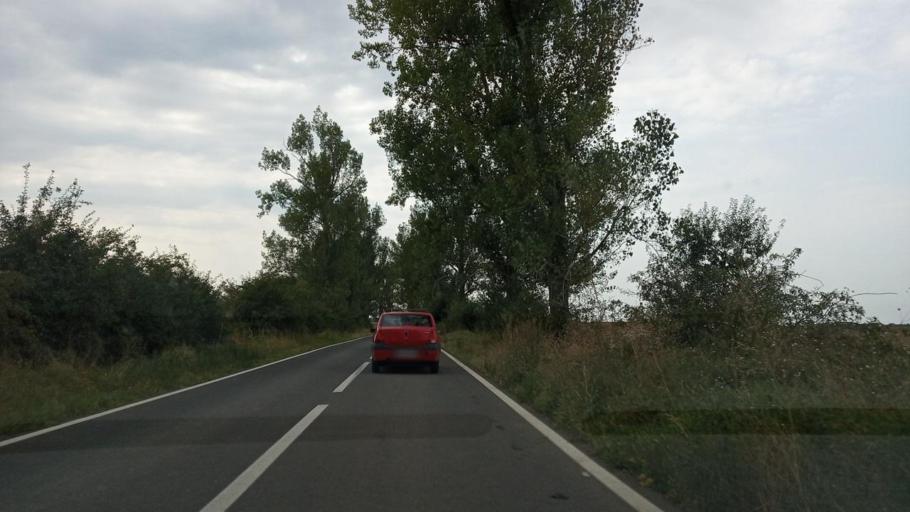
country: RO
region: Giurgiu
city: Gostinari-Vacaresti
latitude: 44.1736
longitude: 26.2244
